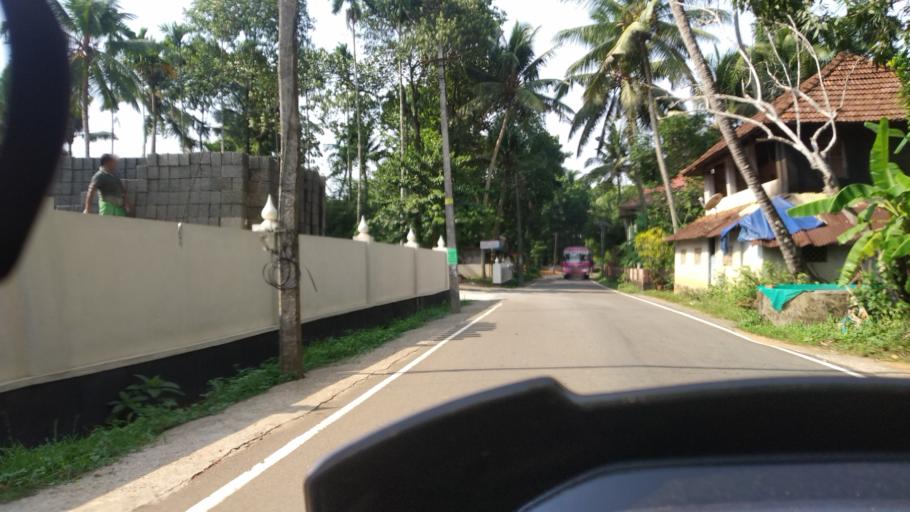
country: IN
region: Kerala
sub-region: Ernakulam
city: Piravam
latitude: 9.8402
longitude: 76.5357
